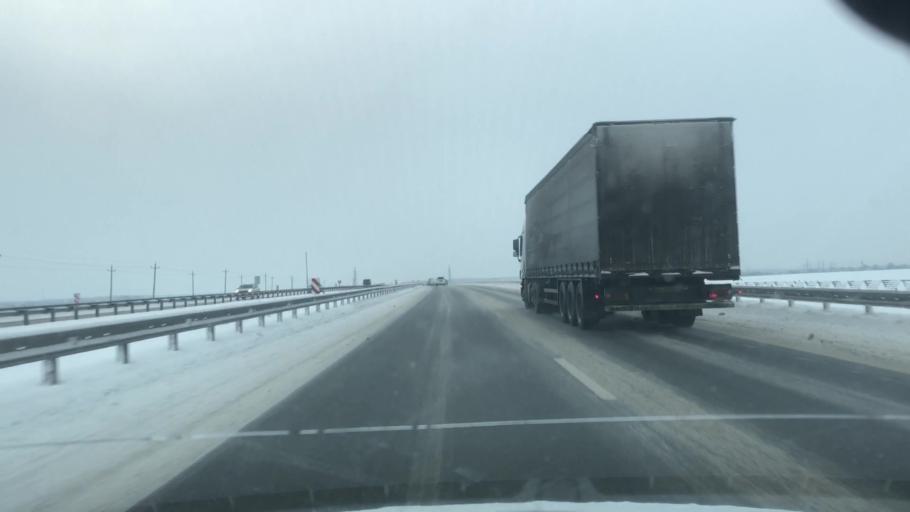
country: RU
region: Moskovskaya
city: Mikhnevo
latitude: 55.1066
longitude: 37.9262
